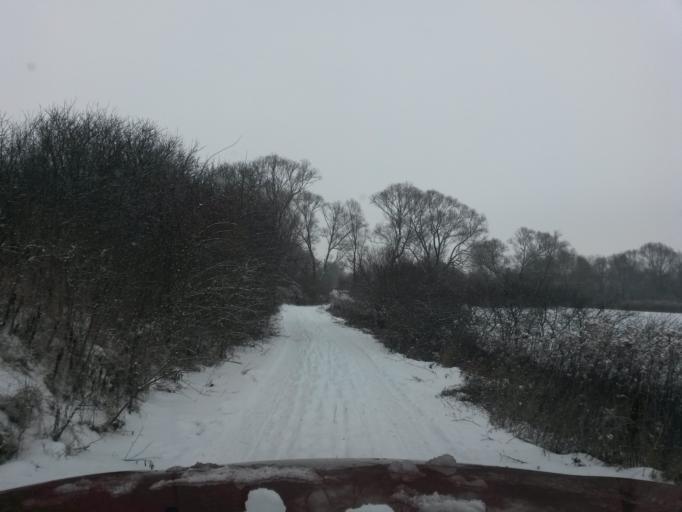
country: SK
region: Kosicky
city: Kosice
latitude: 48.7159
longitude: 21.3327
